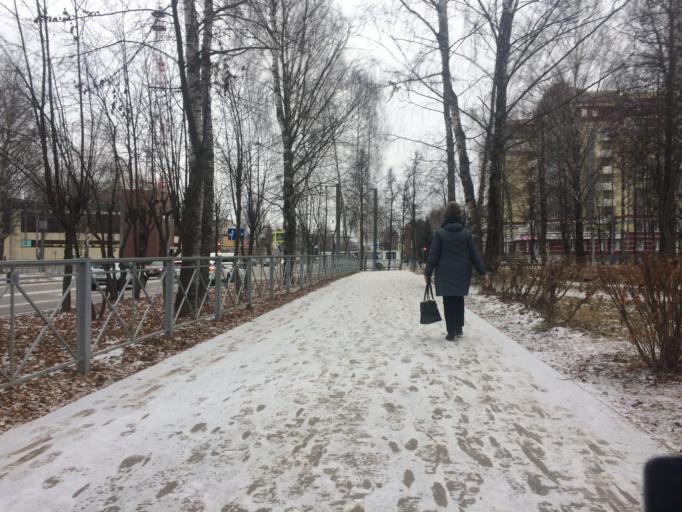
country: RU
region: Mariy-El
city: Yoshkar-Ola
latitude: 56.6451
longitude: 47.8732
